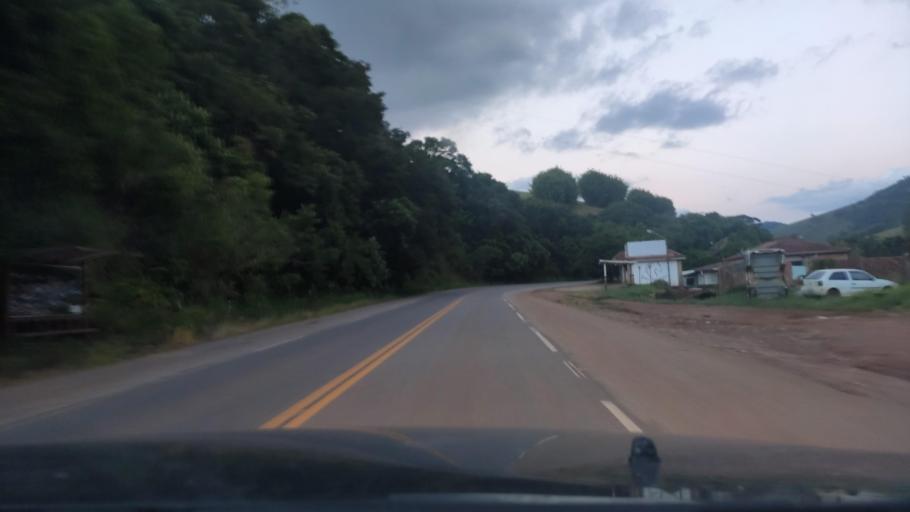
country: BR
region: Sao Paulo
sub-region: Campos Do Jordao
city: Campos do Jordao
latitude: -22.7930
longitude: -45.7455
